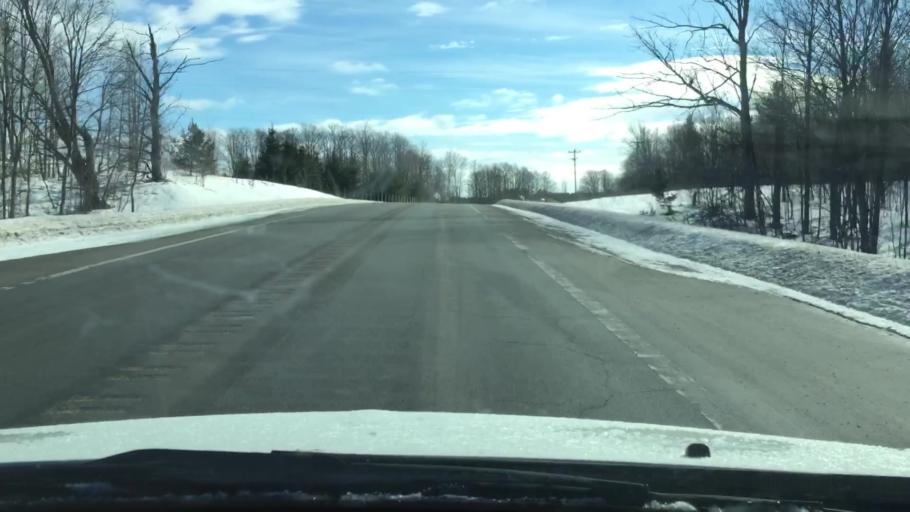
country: US
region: Michigan
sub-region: Antrim County
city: Mancelona
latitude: 44.9477
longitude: -85.0513
